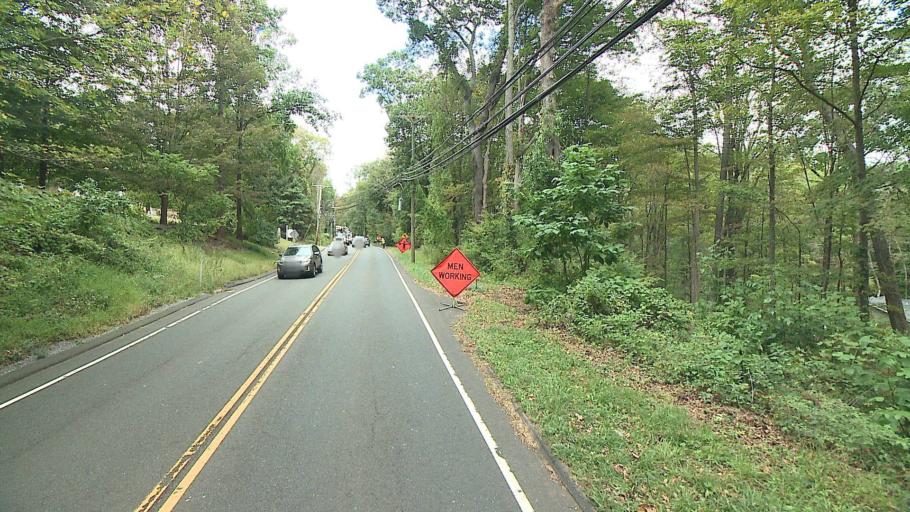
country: US
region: Connecticut
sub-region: Fairfield County
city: Wilton
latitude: 41.1981
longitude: -73.4422
